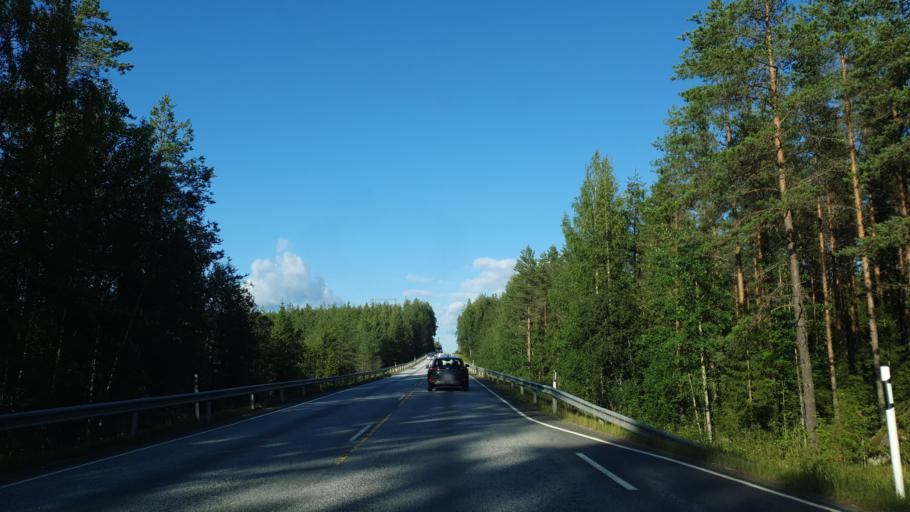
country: FI
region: North Karelia
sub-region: Joensuu
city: Outokumpu
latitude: 62.5251
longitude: 29.0624
